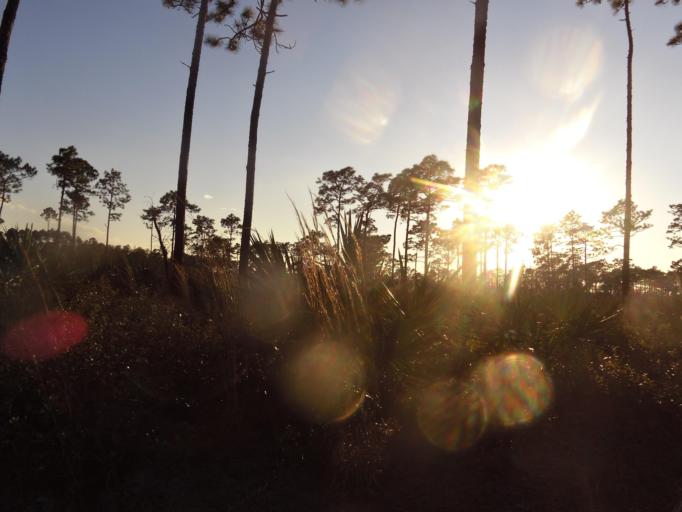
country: US
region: Florida
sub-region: Duval County
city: Atlantic Beach
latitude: 30.4761
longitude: -81.5006
